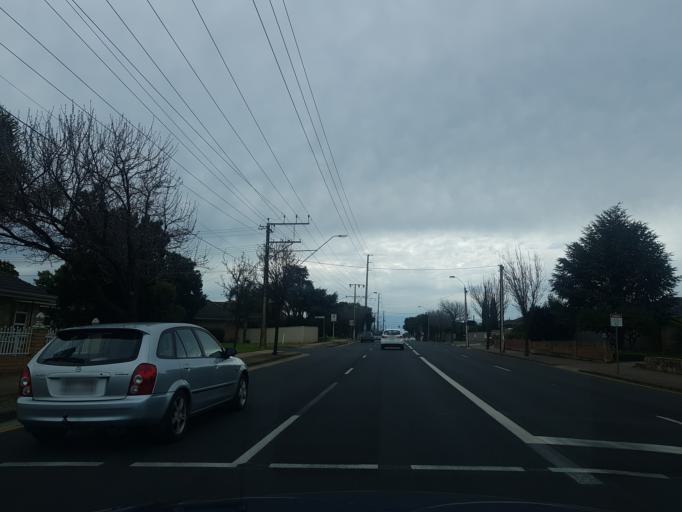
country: AU
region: South Australia
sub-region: Campbelltown
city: Campbelltown
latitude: -34.8849
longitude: 138.6739
